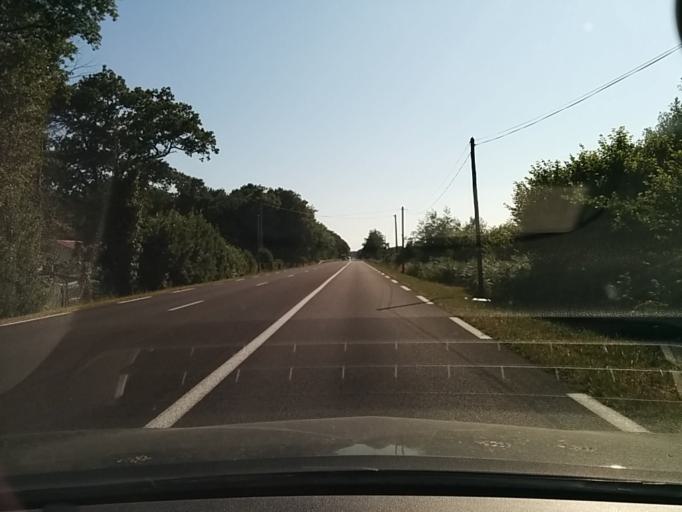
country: FR
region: Aquitaine
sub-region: Departement des Landes
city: Benesse-Maremne
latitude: 43.6257
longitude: -1.3765
